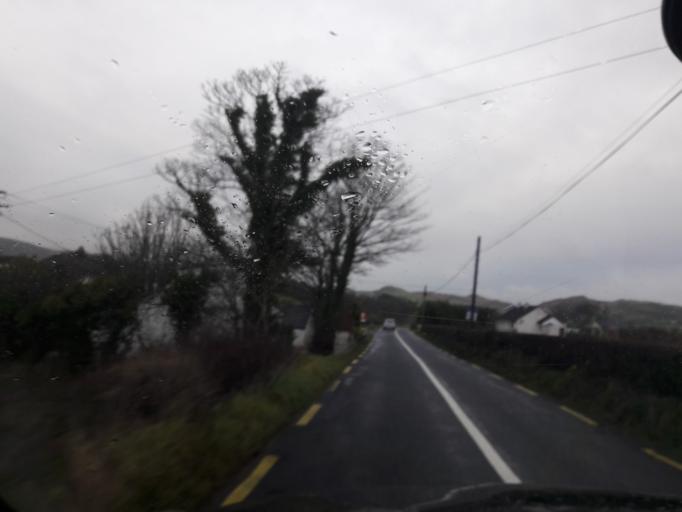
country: IE
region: Ulster
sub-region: County Donegal
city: Ramelton
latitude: 55.1998
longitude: -7.6385
